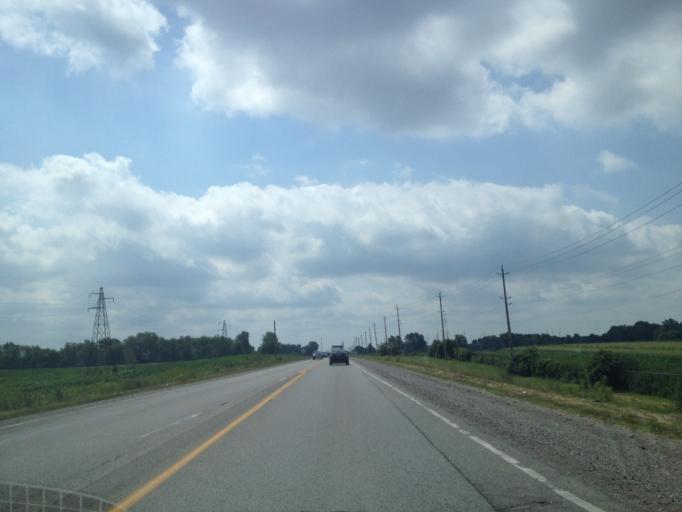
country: CA
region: Ontario
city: London
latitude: 43.0385
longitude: -81.1931
